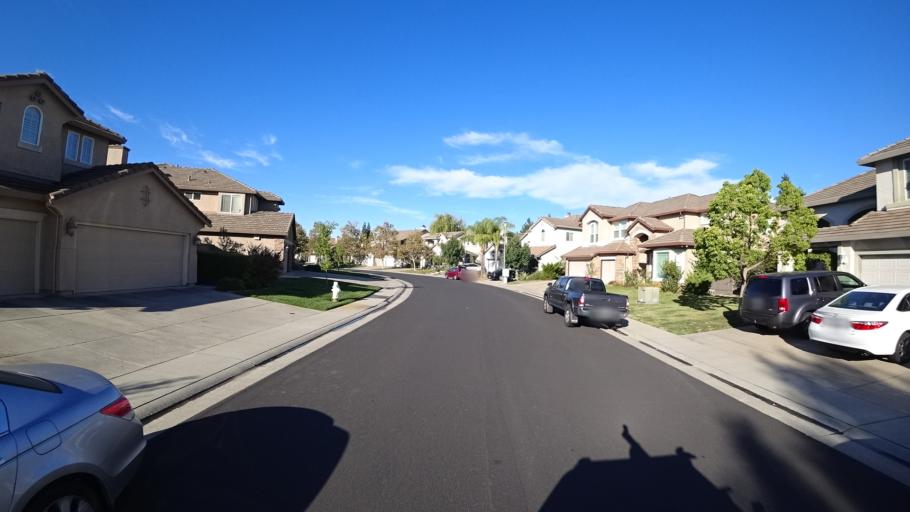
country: US
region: California
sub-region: Sacramento County
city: Laguna
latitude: 38.4004
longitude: -121.4722
